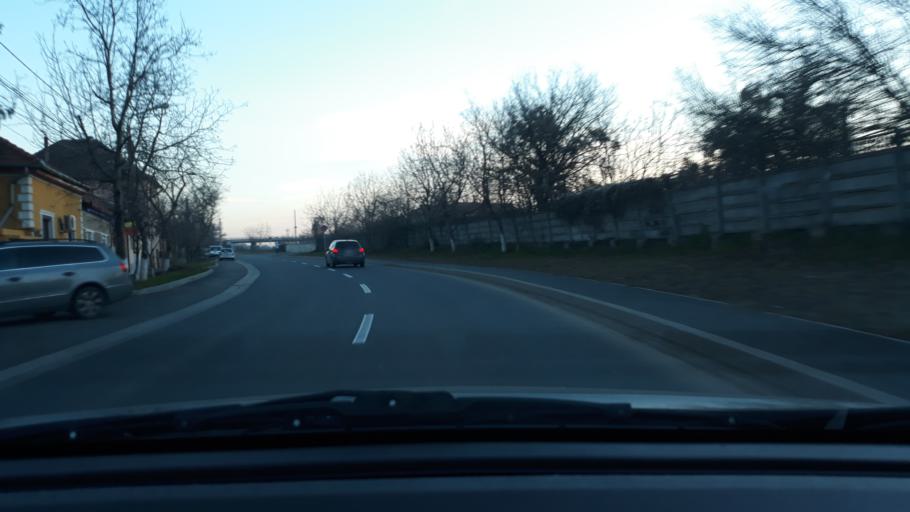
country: RO
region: Bihor
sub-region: Comuna Biharea
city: Oradea
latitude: 47.0806
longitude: 21.9285
